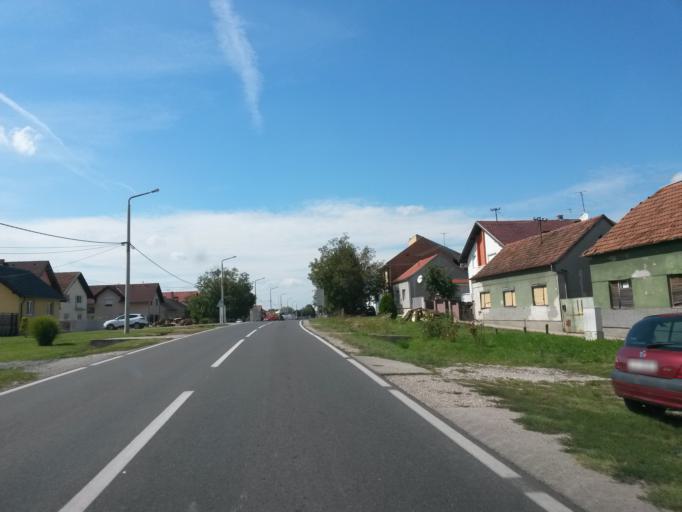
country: HR
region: Vukovarsko-Srijemska
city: Vinkovci
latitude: 45.2806
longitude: 18.8282
